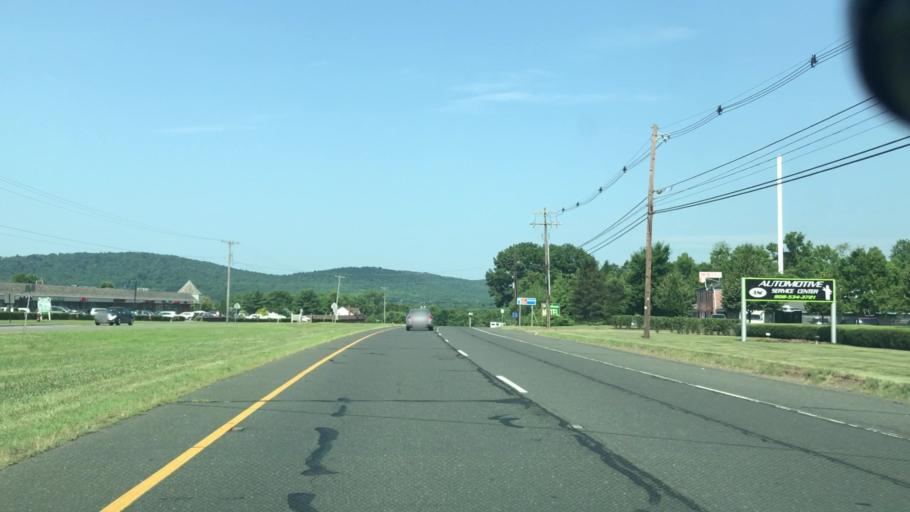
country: US
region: New Jersey
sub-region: Hunterdon County
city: Whitehouse Station
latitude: 40.6190
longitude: -74.7557
